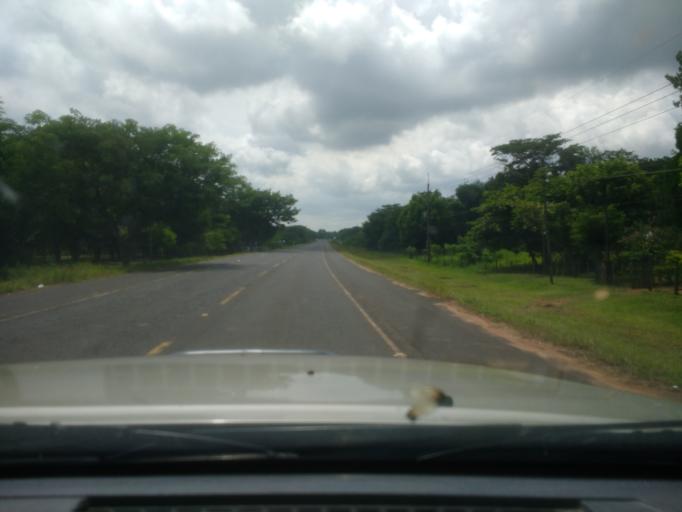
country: PY
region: San Pedro
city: Puerto Rosario
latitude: -24.4178
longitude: -57.1025
